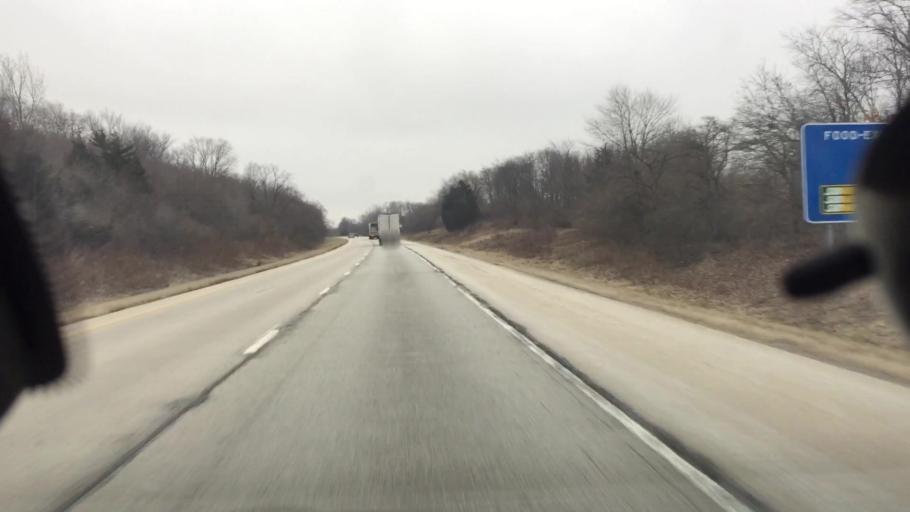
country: US
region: Illinois
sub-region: Henry County
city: Orion
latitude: 41.2022
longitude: -90.3331
